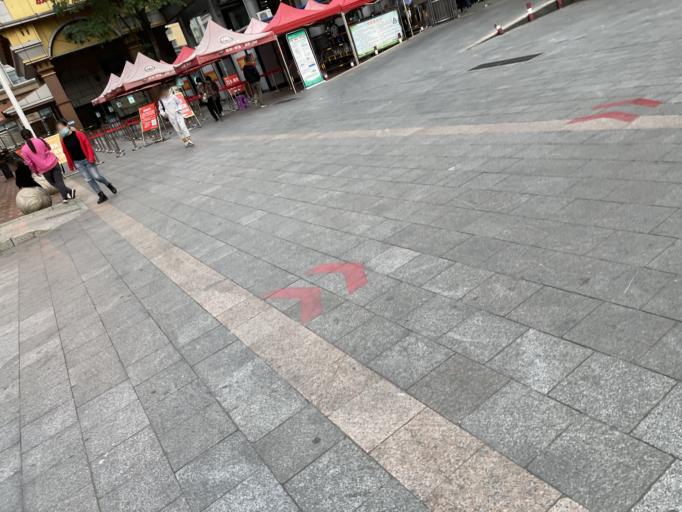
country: CN
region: Guangxi Zhuangzu Zizhiqu
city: Qinzhou
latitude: 21.9648
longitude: 108.6275
